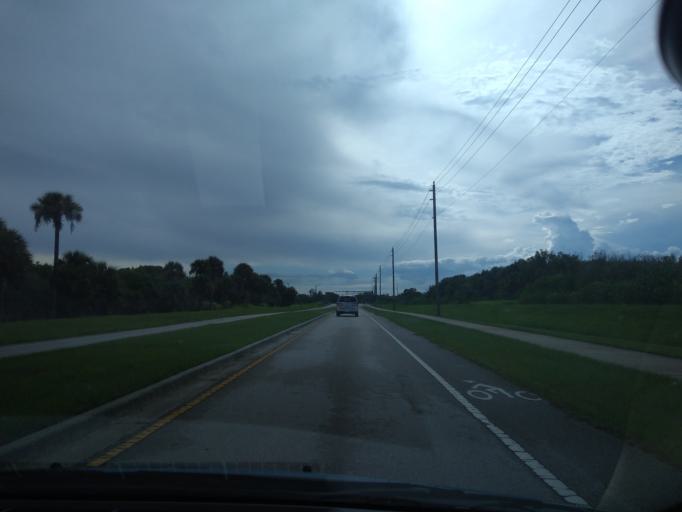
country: US
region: Florida
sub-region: Indian River County
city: West Vero Corridor
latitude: 27.6317
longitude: -80.4600
